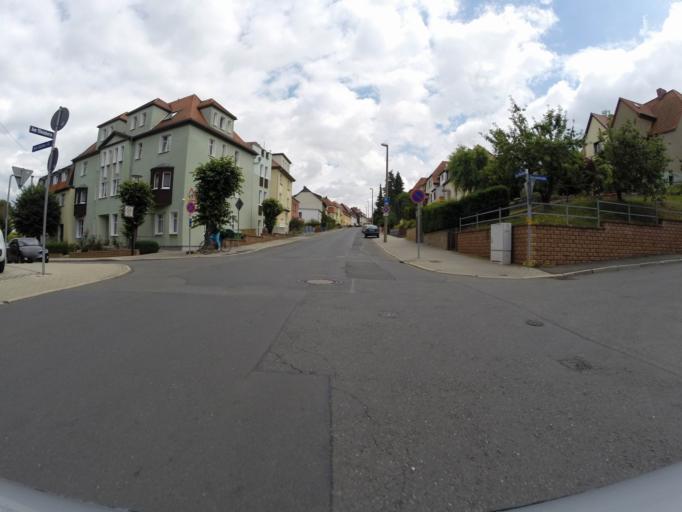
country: DE
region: Thuringia
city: Jena
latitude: 50.9321
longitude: 11.6075
